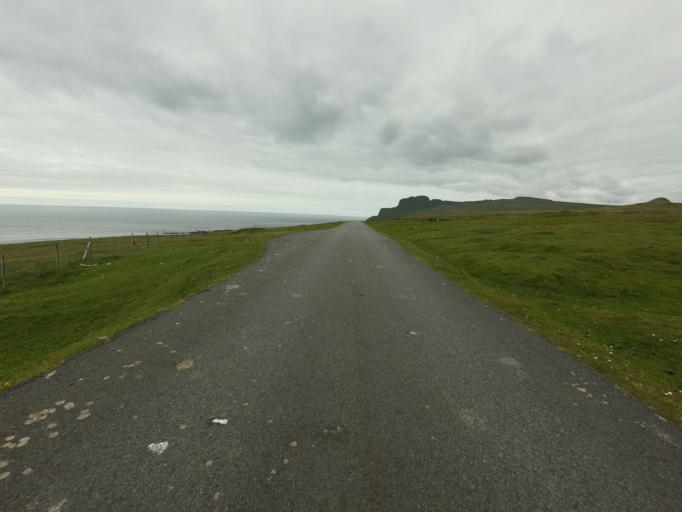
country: FO
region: Suduroy
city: Vagur
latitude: 61.3967
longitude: -6.6911
